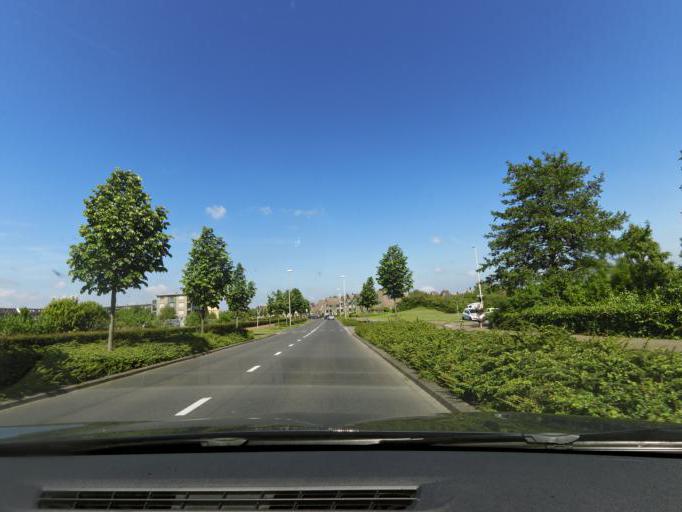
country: NL
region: South Holland
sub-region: Gemeente Hellevoetsluis
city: Hellevoetsluis
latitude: 51.8266
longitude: 4.1584
